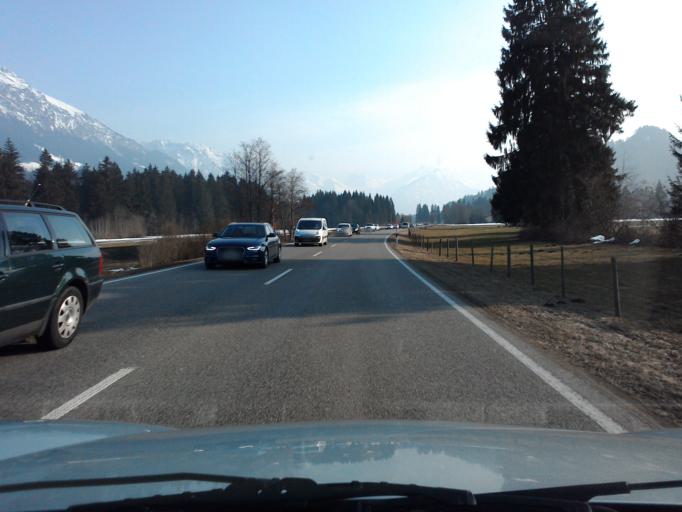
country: DE
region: Bavaria
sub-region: Swabia
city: Obermaiselstein
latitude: 47.4531
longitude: 10.2720
